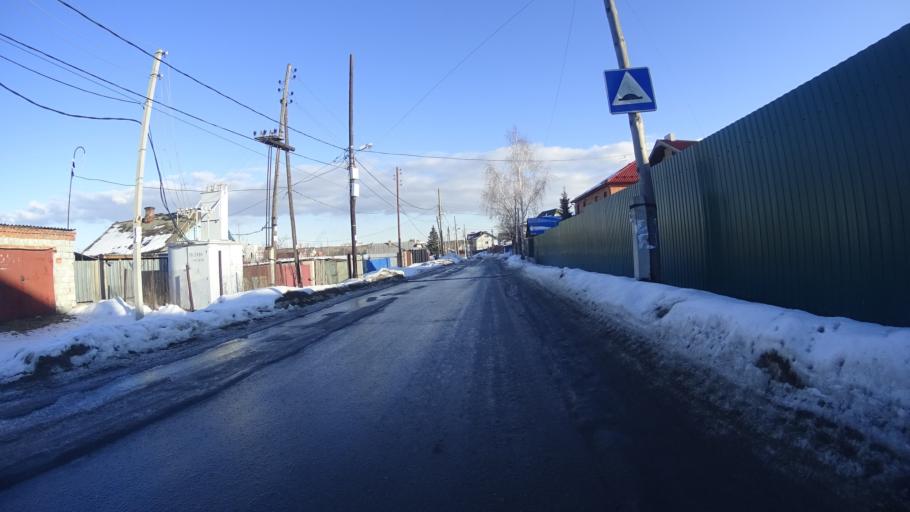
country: RU
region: Chelyabinsk
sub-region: Gorod Chelyabinsk
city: Chelyabinsk
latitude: 55.1547
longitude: 61.3088
